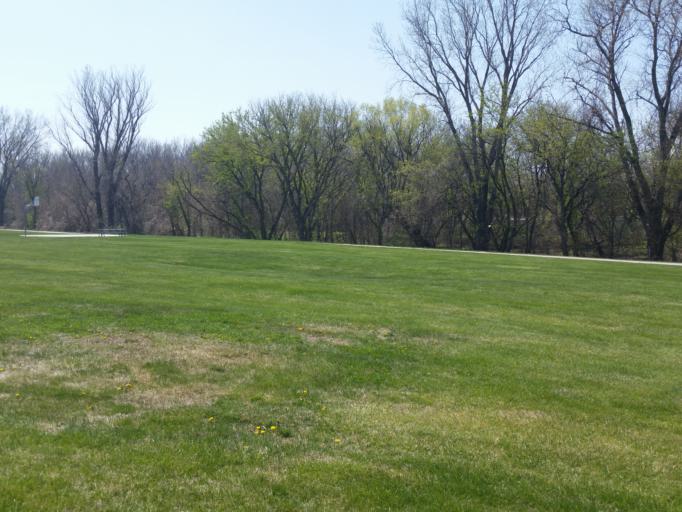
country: US
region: Nebraska
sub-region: Sarpy County
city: Offutt Air Force Base
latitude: 41.1475
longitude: -95.9340
